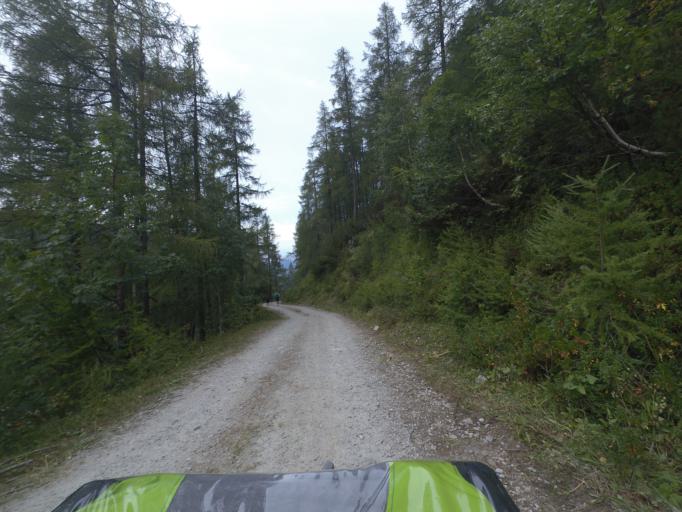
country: AT
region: Salzburg
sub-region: Politischer Bezirk Sankt Johann im Pongau
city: Untertauern
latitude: 47.2945
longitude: 13.5838
